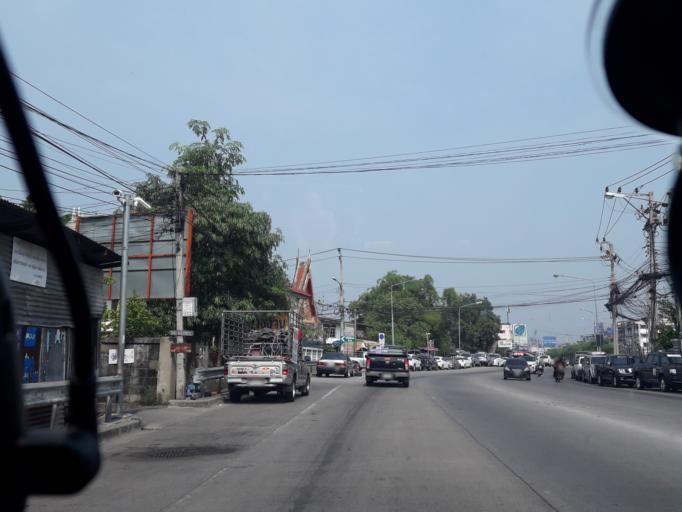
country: TH
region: Bangkok
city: Khan Na Yao
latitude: 13.8185
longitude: 100.6990
